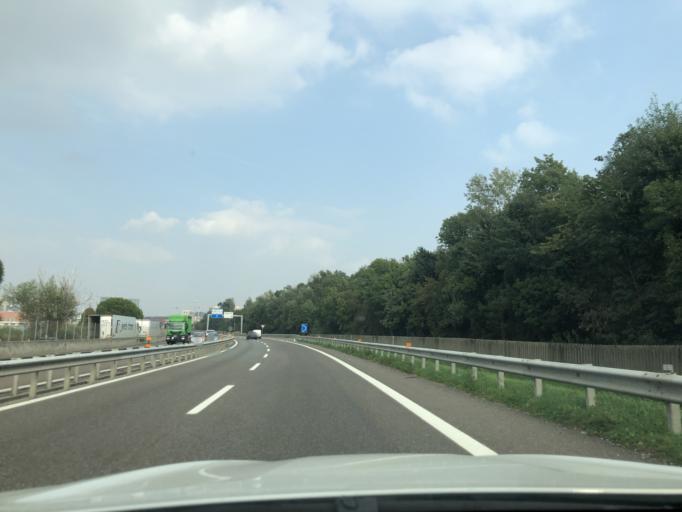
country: IT
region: Lombardy
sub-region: Citta metropolitana di Milano
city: Figino
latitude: 45.4986
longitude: 9.0857
